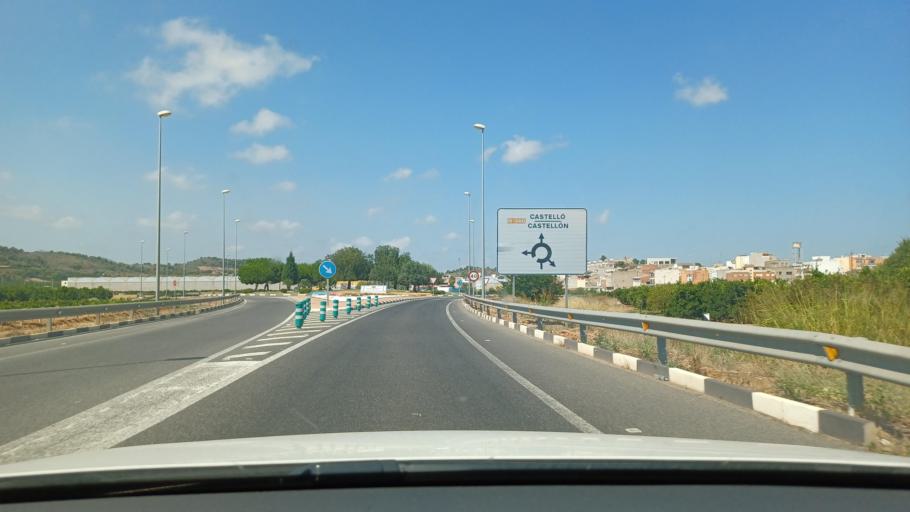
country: ES
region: Valencia
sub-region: Provincia de Castello
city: Almenara
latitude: 39.7652
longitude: -0.2100
